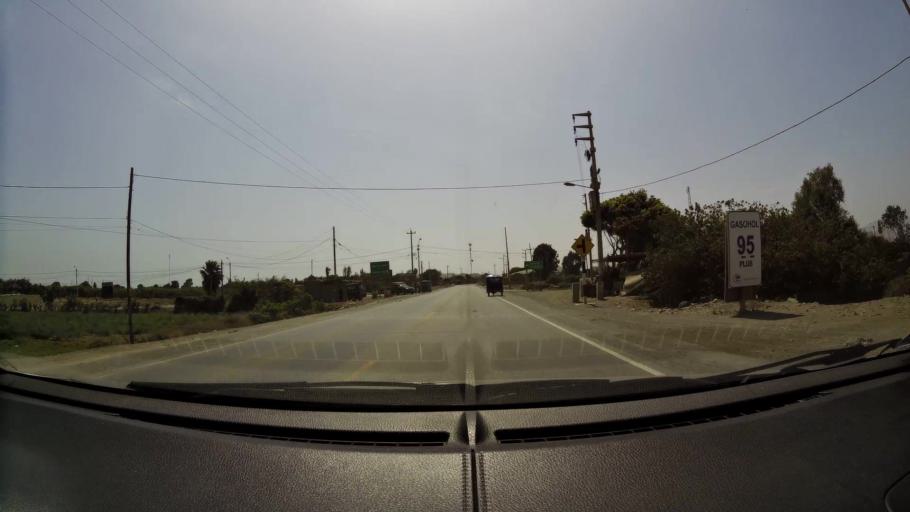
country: PE
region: Ancash
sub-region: Provincia de Huarmey
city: Huarmey
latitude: -10.0739
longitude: -78.1544
